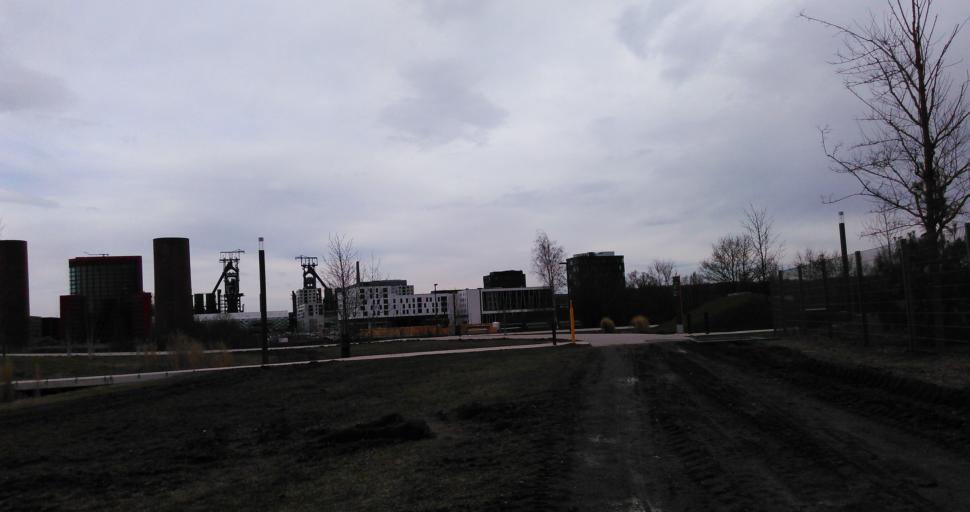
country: LU
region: Luxembourg
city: Belvaux
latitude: 49.5050
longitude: 5.9364
